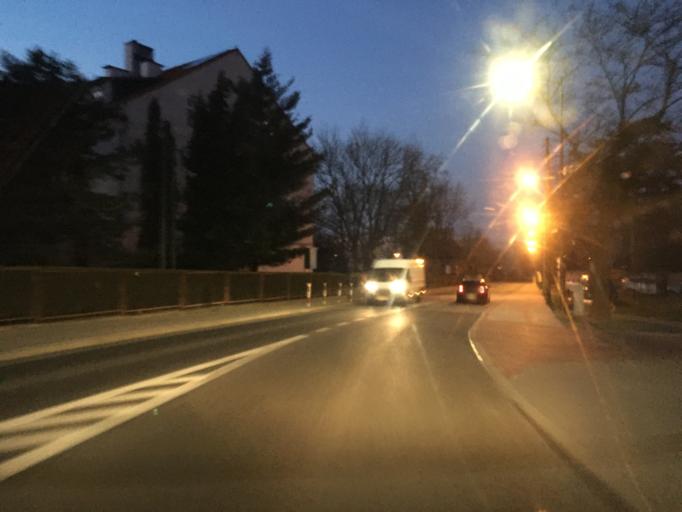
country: PL
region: Lower Silesian Voivodeship
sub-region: Powiat dzierzoniowski
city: Bielawa
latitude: 50.6910
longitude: 16.6231
